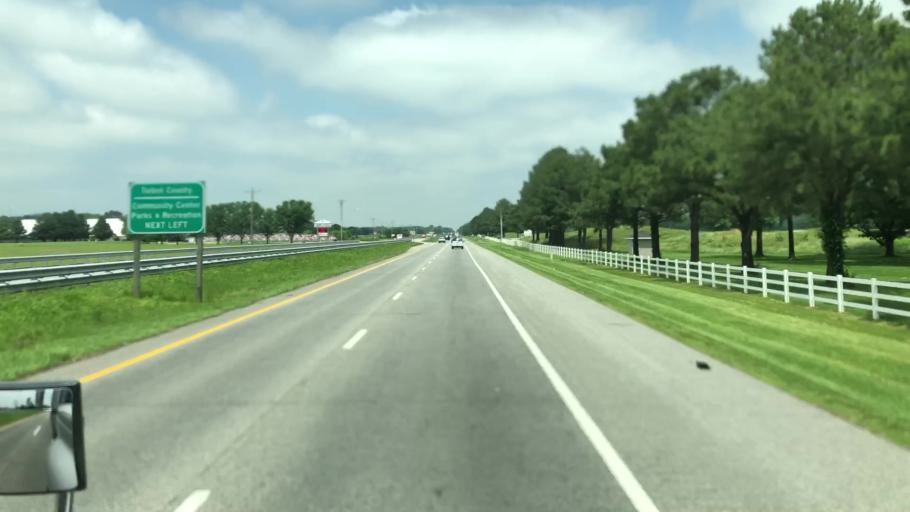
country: US
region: Maryland
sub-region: Talbot County
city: Easton
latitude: 38.8223
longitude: -76.0600
